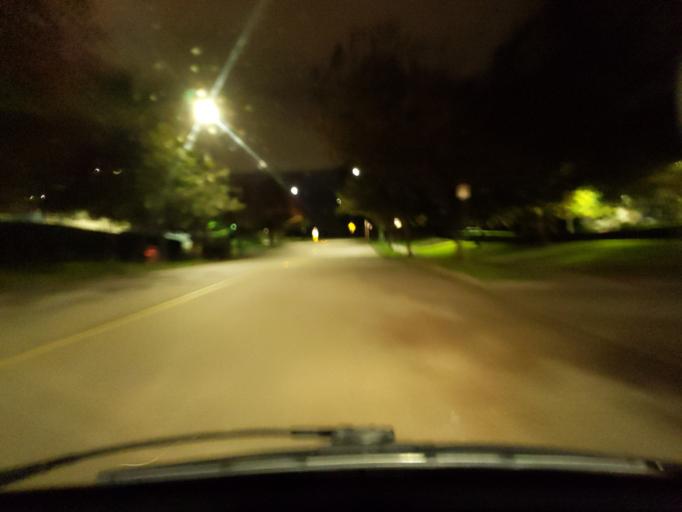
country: CA
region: British Columbia
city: Burnaby
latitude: 49.2598
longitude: -123.0111
